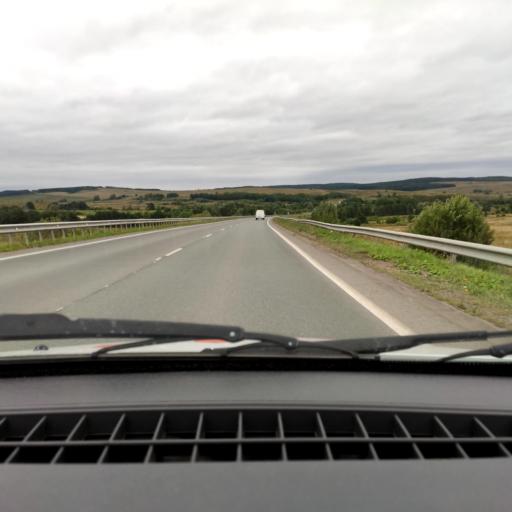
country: RU
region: Bashkortostan
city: Blagoveshchensk
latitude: 55.1033
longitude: 55.8241
